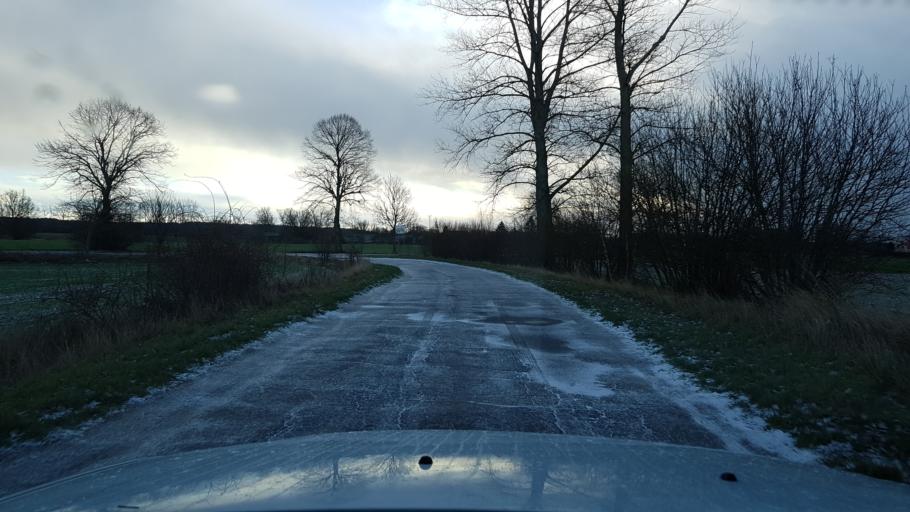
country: PL
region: West Pomeranian Voivodeship
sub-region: Powiat gryficki
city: Brojce
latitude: 54.0375
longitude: 15.3569
